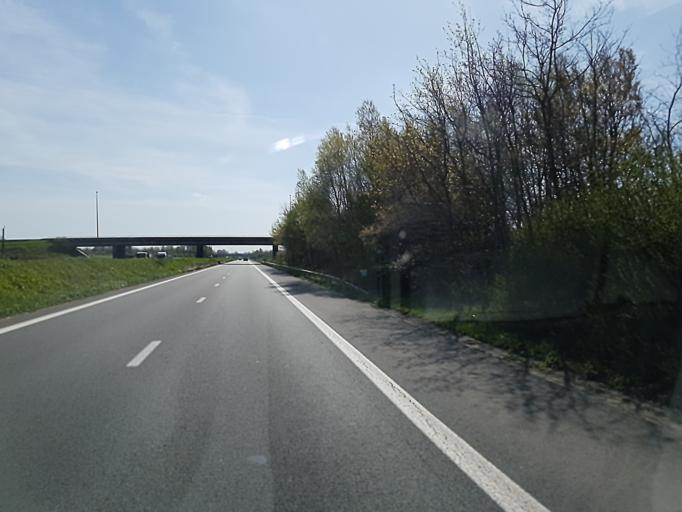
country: BE
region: Flanders
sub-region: Provincie West-Vlaanderen
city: Kortrijk
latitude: 50.7788
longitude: 3.2511
